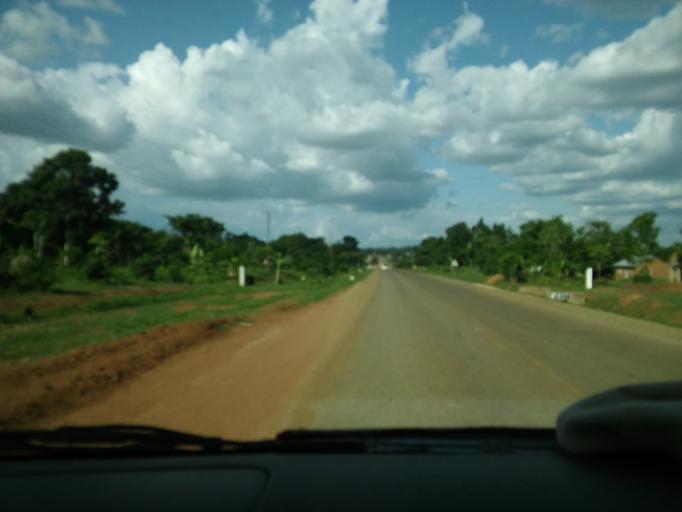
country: UG
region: Eastern Region
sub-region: Budaka District
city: Budaka
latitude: 1.0167
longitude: 33.8664
